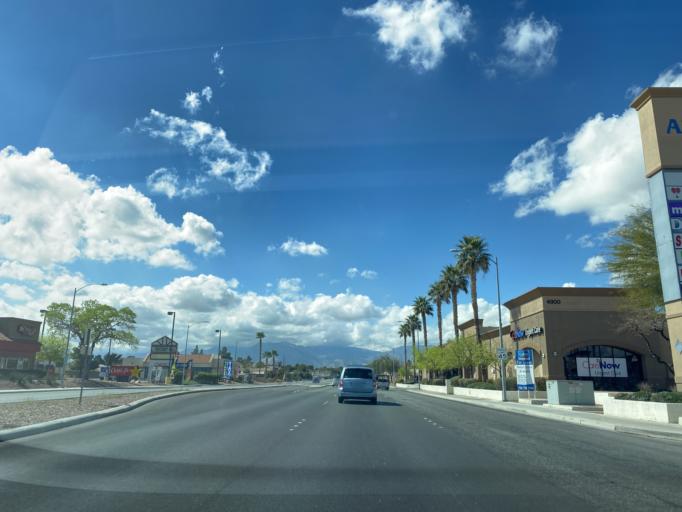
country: US
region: Nevada
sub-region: Clark County
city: Las Vegas
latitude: 36.2389
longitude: -115.2086
